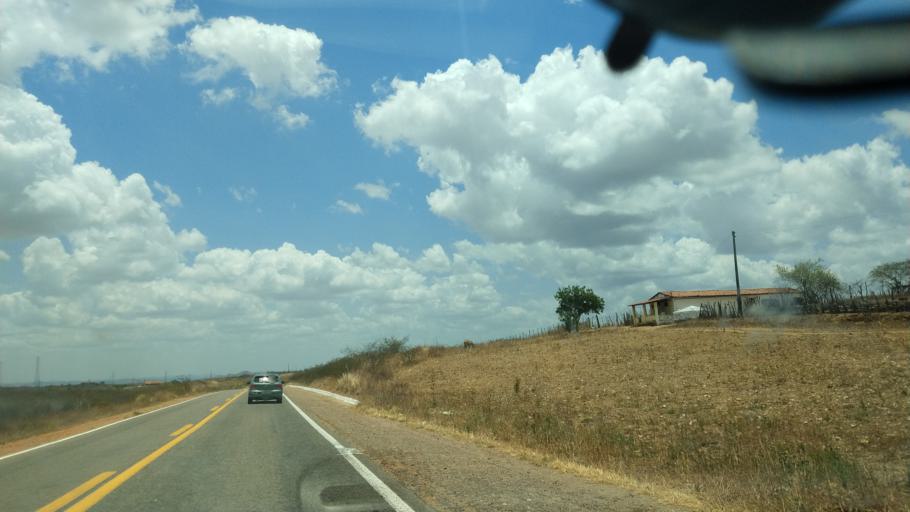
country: BR
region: Rio Grande do Norte
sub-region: Cerro Cora
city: Cerro Cora
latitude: -6.1892
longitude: -36.2496
